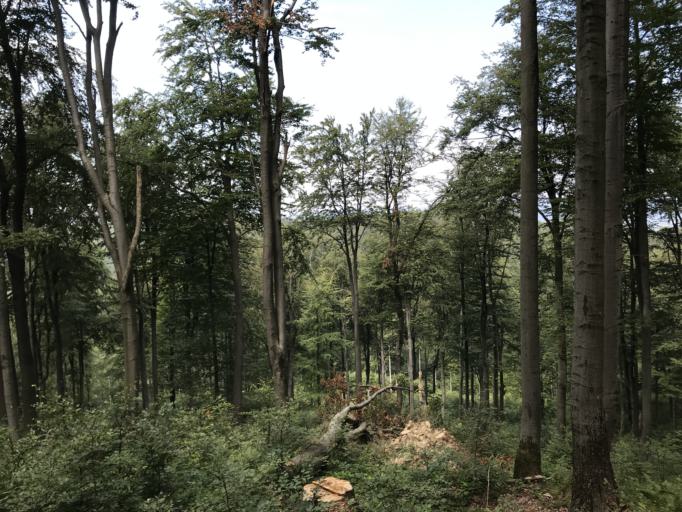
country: PL
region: Lesser Poland Voivodeship
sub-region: Powiat gorlicki
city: Uscie Gorlickie
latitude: 49.4481
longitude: 21.2173
